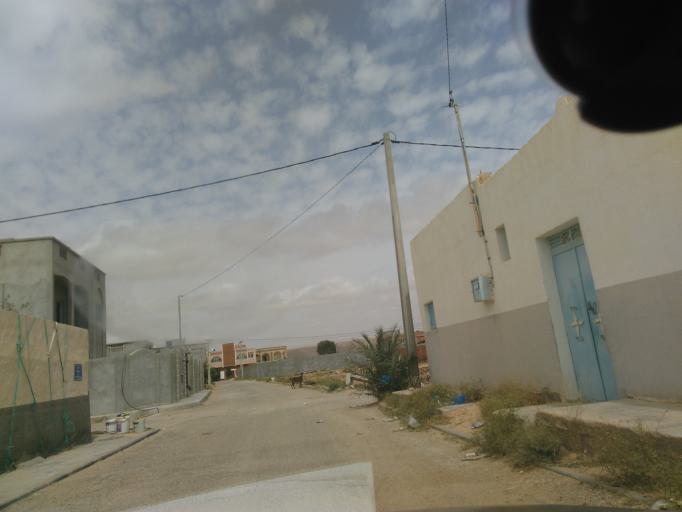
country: TN
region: Tataouine
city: Tataouine
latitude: 32.9522
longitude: 10.4665
